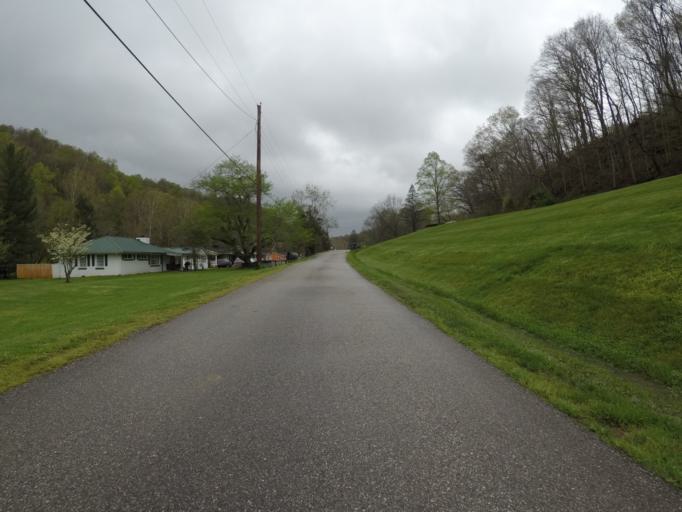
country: US
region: Ohio
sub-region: Lawrence County
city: Burlington
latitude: 38.3745
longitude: -82.4930
